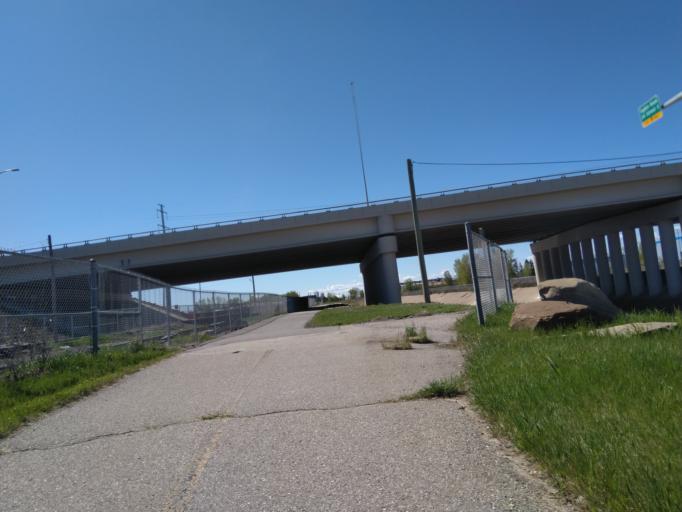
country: CA
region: Alberta
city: Calgary
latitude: 50.9798
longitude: -113.9931
